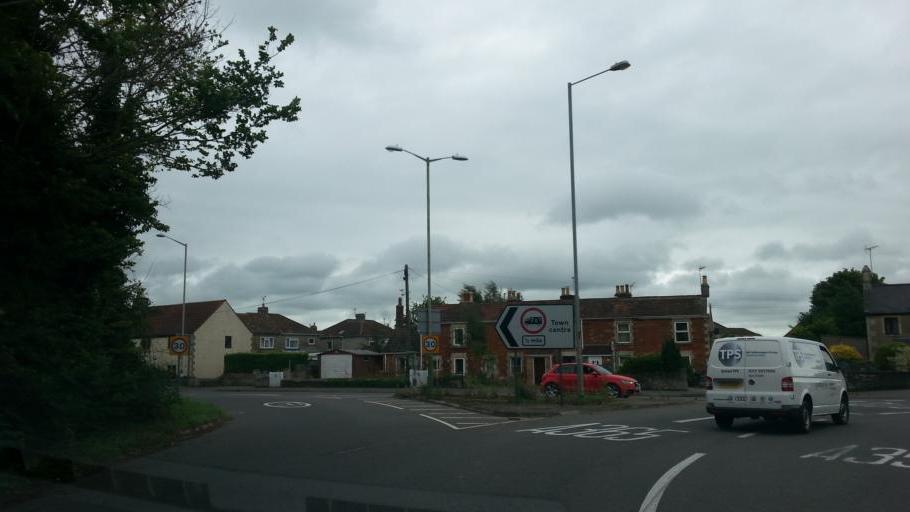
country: GB
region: England
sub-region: Wiltshire
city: Melksham
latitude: 51.3652
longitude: -2.1415
